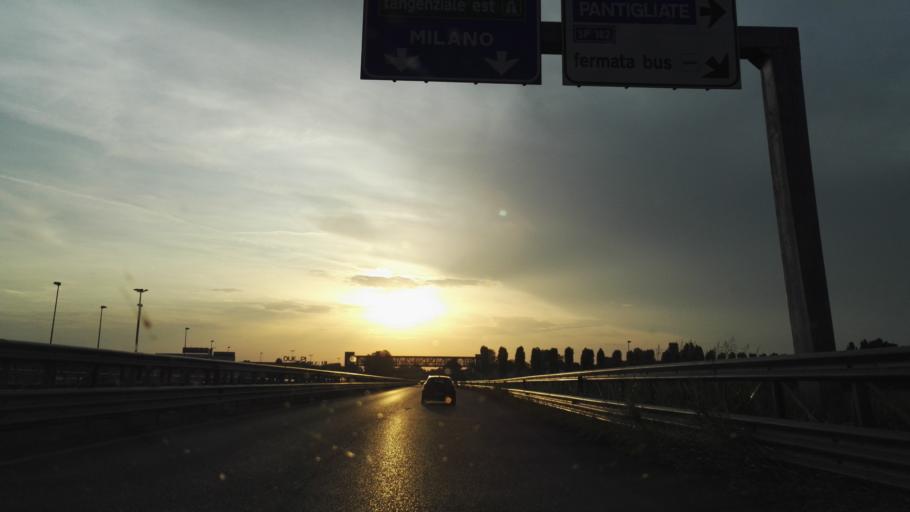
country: IT
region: Lombardy
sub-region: Citta metropolitana di Milano
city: Mombretto
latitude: 45.4298
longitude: 9.3668
